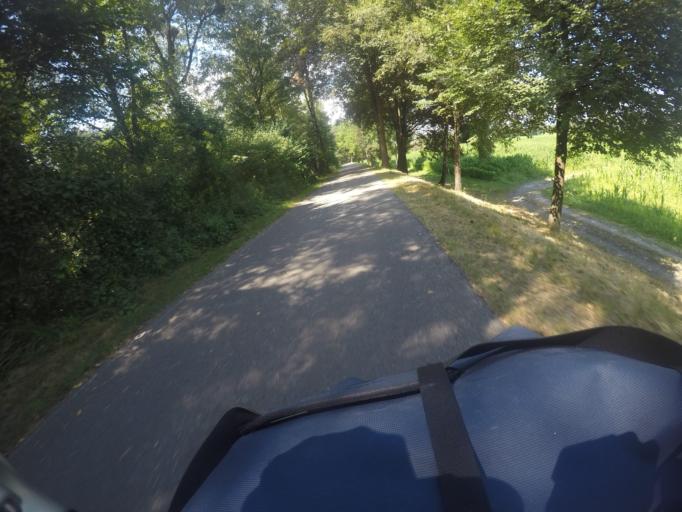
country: CH
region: Saint Gallen
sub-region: Wahlkreis Rheintal
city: Diepoldsau
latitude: 47.3887
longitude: 9.6764
